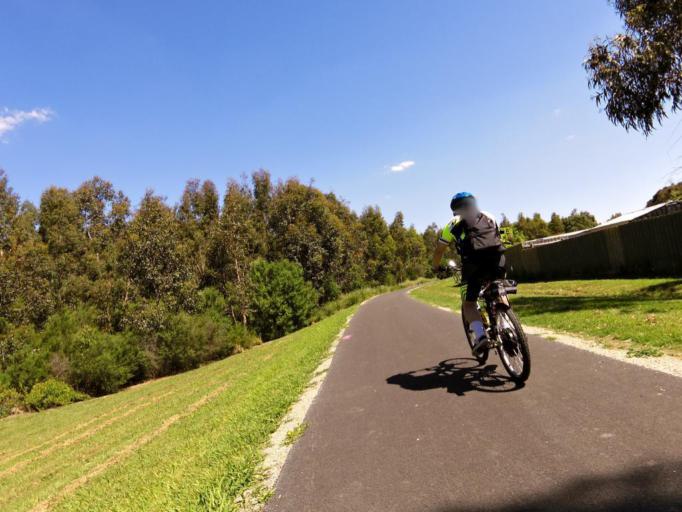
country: AU
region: Victoria
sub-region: Knox
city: Knoxfield
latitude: -37.8985
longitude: 145.2681
